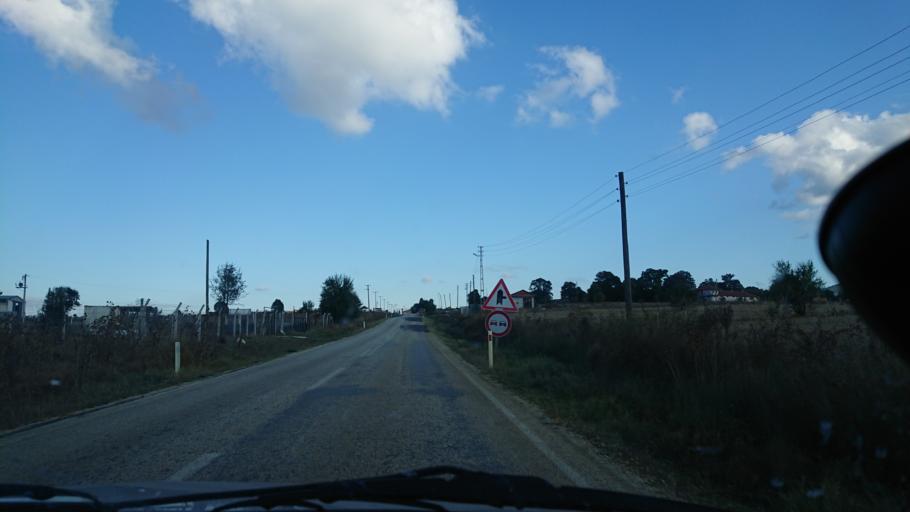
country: TR
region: Bilecik
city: Pazaryeri
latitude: 40.0035
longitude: 29.8806
